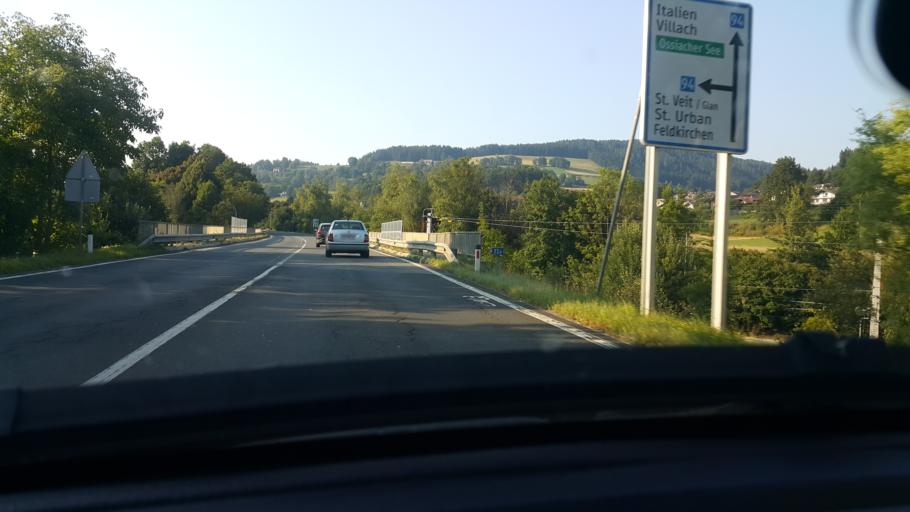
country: AT
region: Carinthia
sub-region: Politischer Bezirk Feldkirchen
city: Feldkirchen in Karnten
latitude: 46.7207
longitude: 14.1053
